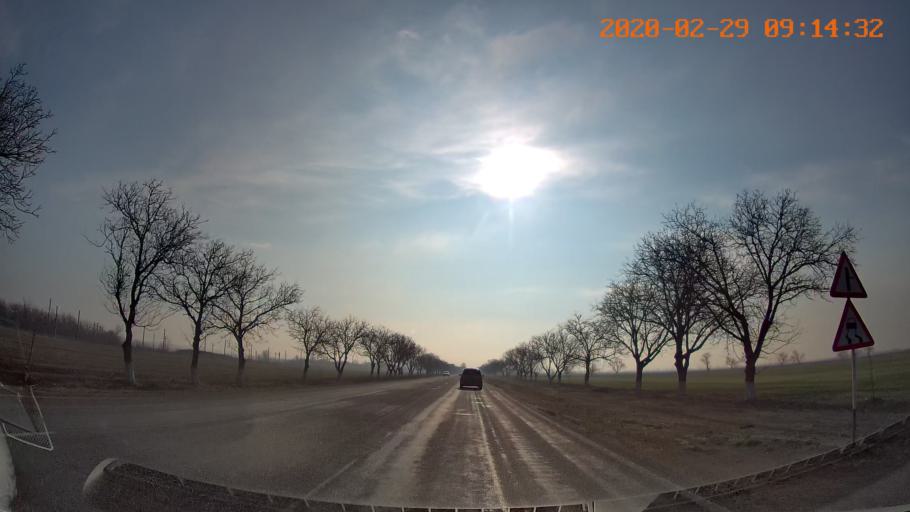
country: MD
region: Telenesti
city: Pervomaisc
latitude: 46.8079
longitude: 29.8543
